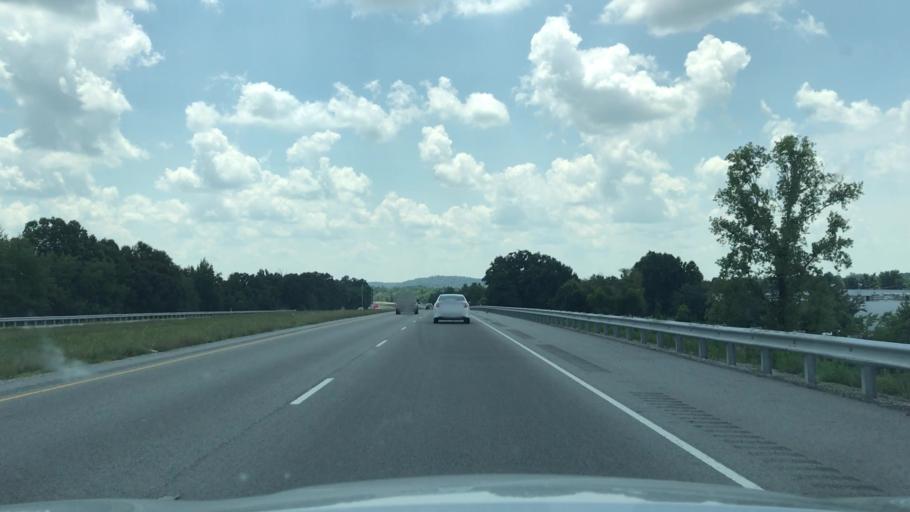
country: US
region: Tennessee
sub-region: Putnam County
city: Algood
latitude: 36.1895
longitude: -85.4620
